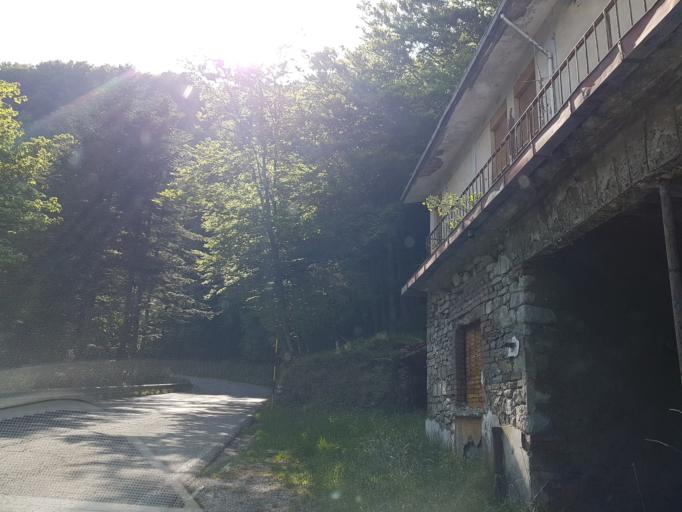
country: IT
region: Emilia-Romagna
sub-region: Forli-Cesena
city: San Piero in Bagno
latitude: 43.8034
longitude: 11.9147
